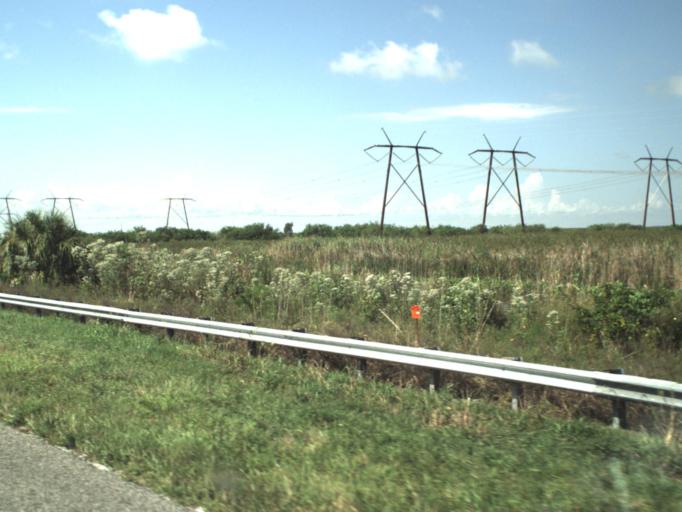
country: US
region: Florida
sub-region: Broward County
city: Weston
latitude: 26.1981
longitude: -80.4537
